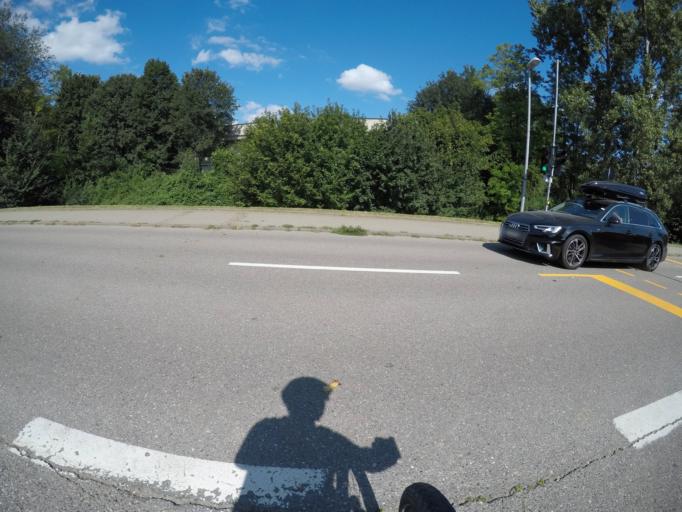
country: DE
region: Baden-Wuerttemberg
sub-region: Regierungsbezirk Stuttgart
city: Grossbettlingen
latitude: 48.6151
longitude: 9.3101
